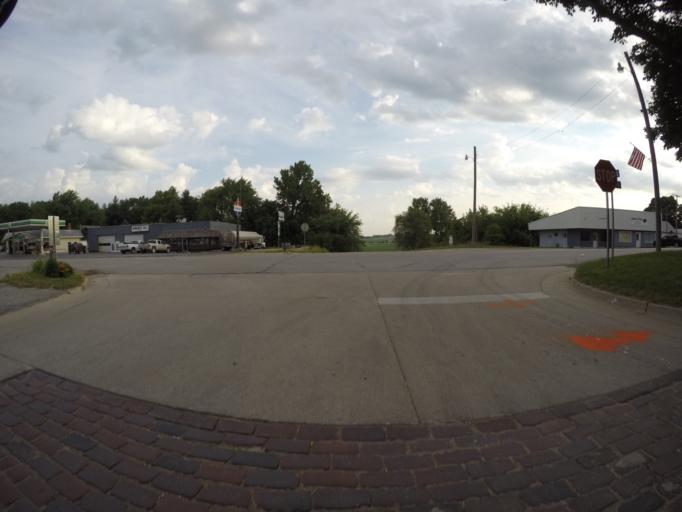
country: US
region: Kansas
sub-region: Doniphan County
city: Troy
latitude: 39.7897
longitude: -95.0896
